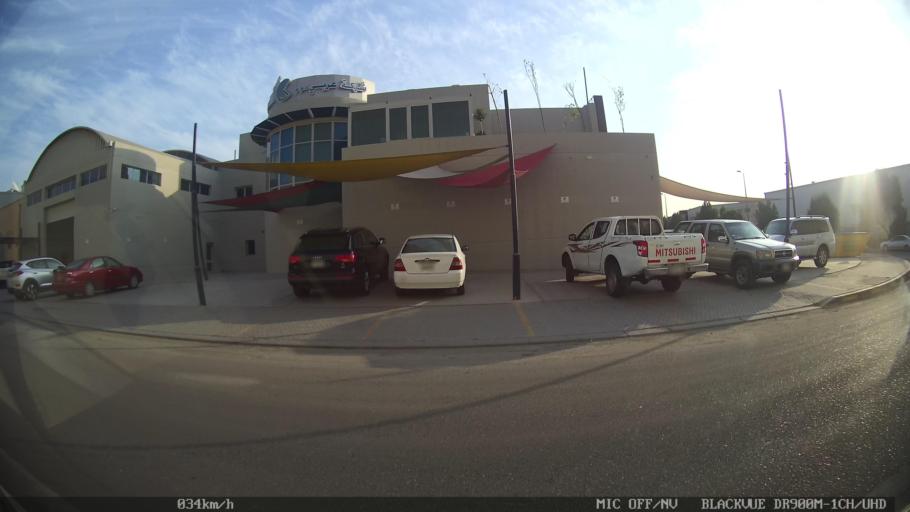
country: KW
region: Al Farwaniyah
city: Janub as Surrah
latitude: 29.2399
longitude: 48.0053
